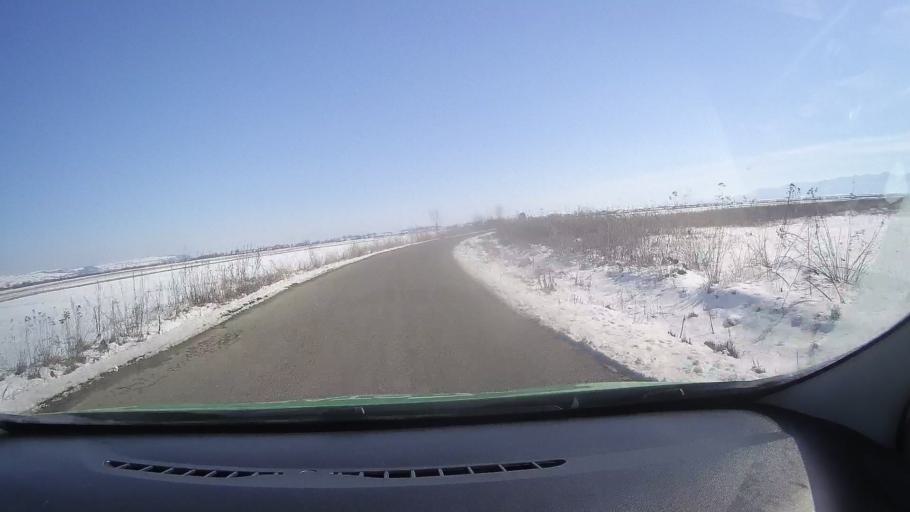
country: RO
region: Brasov
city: Fogarasch
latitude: 45.8181
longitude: 24.9884
